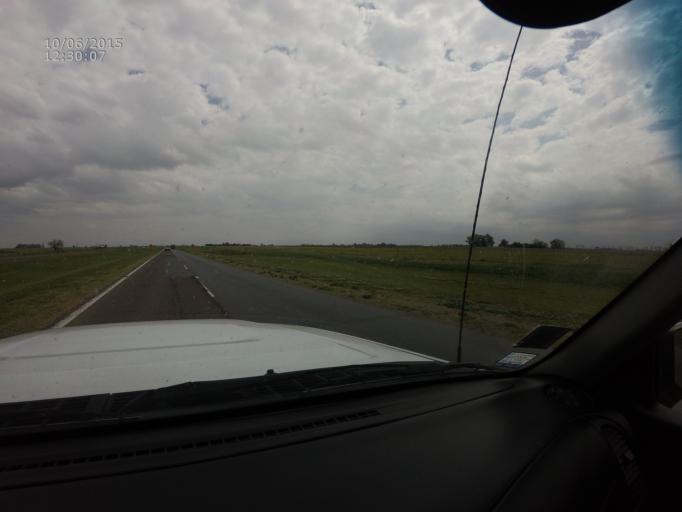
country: AR
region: Santa Fe
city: Carcarana
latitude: -32.8897
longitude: -61.0954
